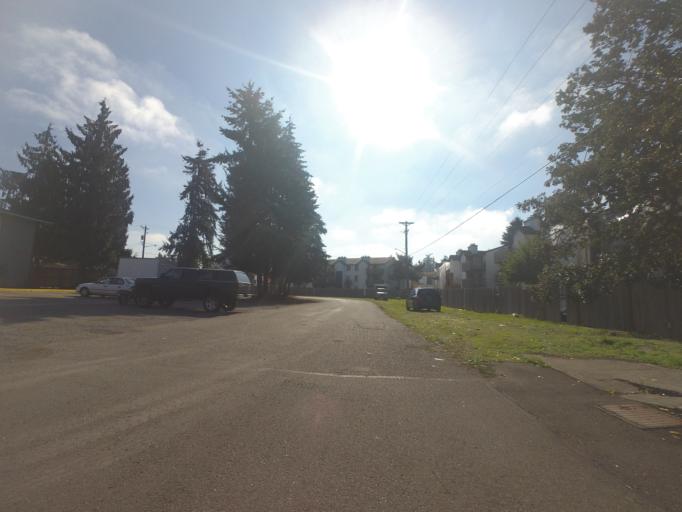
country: US
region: Washington
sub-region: Pierce County
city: Lakewood
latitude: 47.1859
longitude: -122.5163
